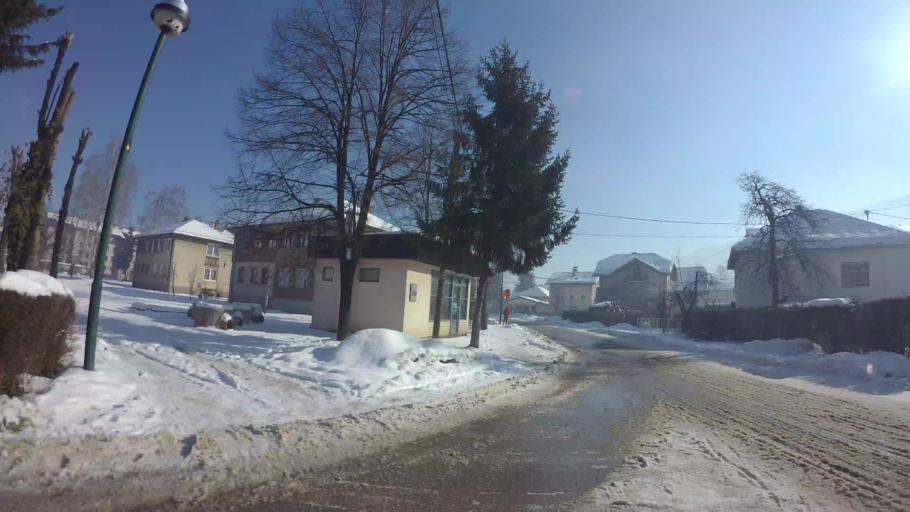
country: BA
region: Federation of Bosnia and Herzegovina
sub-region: Kanton Sarajevo
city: Sarajevo
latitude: 43.7985
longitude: 18.3083
